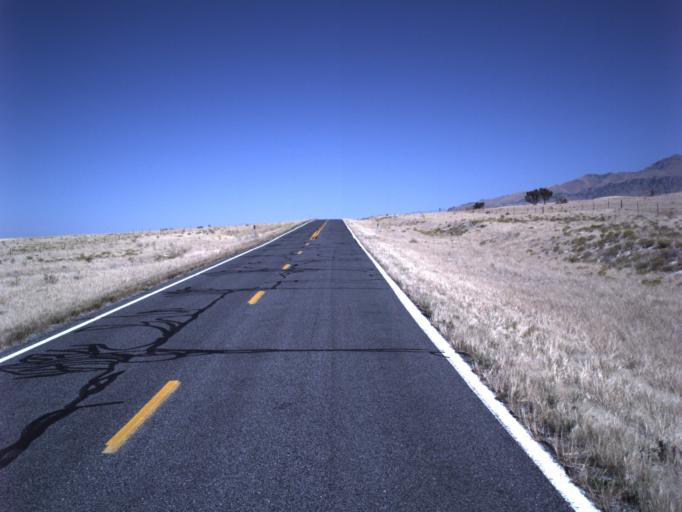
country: US
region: Utah
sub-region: Tooele County
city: Grantsville
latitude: 40.5773
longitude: -112.7272
